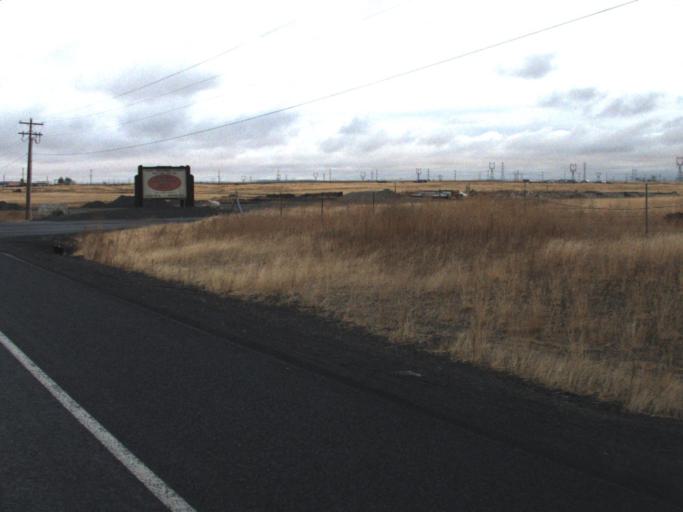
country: US
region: Washington
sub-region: Lincoln County
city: Davenport
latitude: 47.7558
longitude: -118.4974
